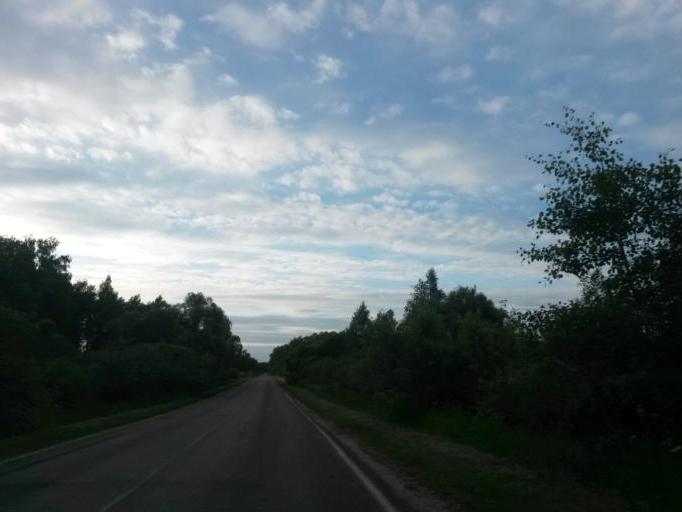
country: RU
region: Moskovskaya
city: Melikhovo
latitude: 55.2025
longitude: 37.6949
